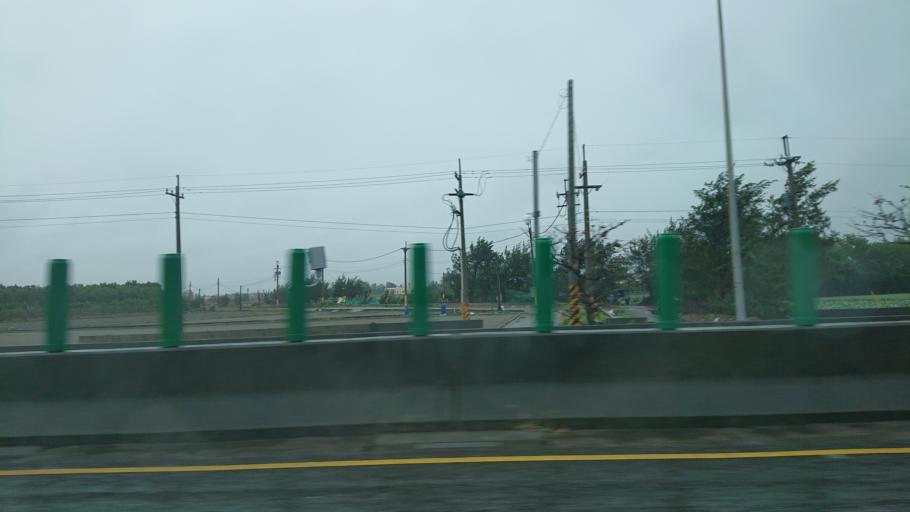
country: TW
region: Taiwan
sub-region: Chiayi
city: Taibao
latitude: 23.7275
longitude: 120.2202
